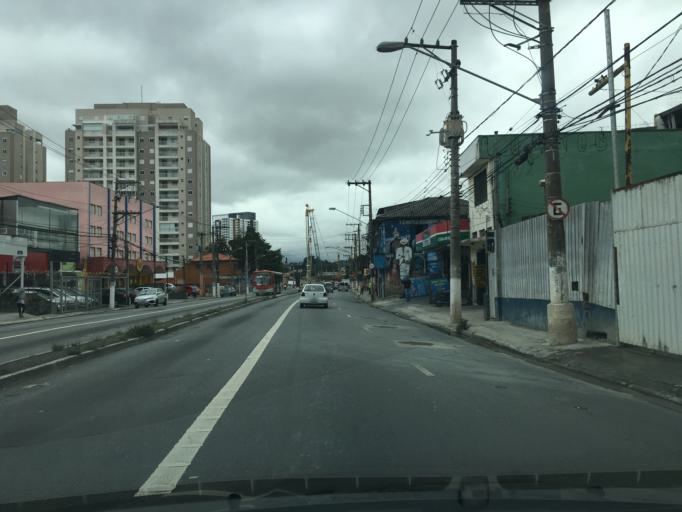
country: BR
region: Sao Paulo
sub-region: Taboao Da Serra
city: Taboao da Serra
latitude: -23.5980
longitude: -46.7407
